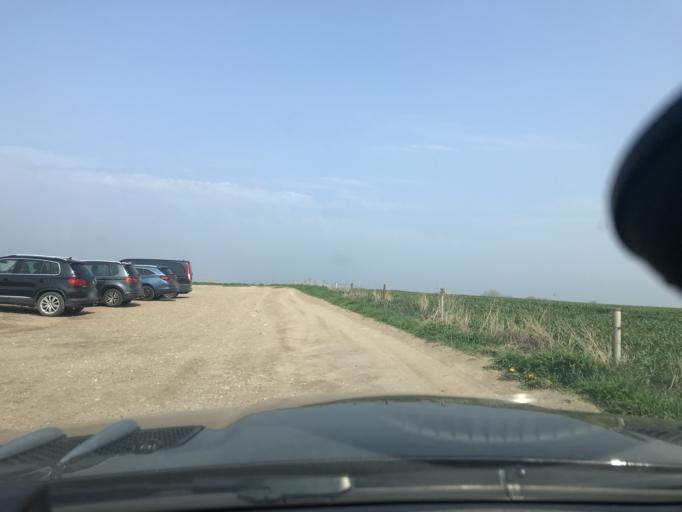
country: DE
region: Schleswig-Holstein
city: Gremersdorf
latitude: 54.3707
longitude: 10.9137
